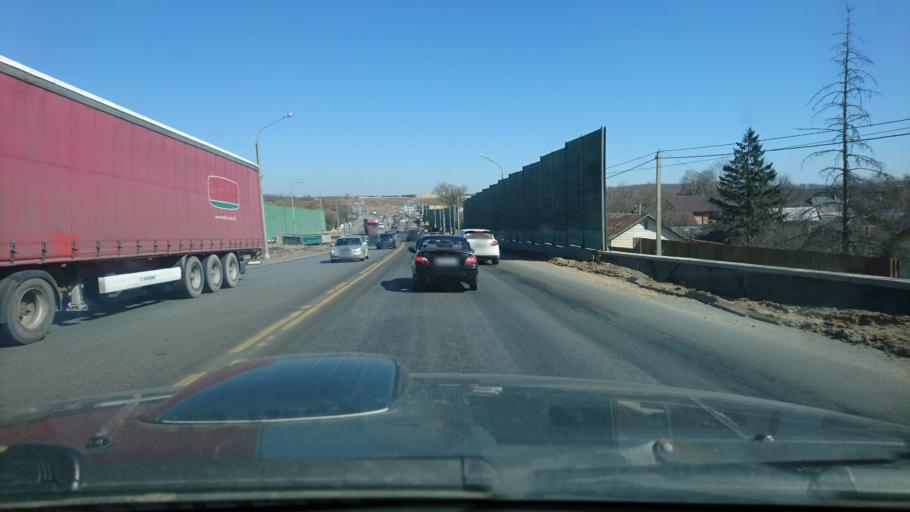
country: RU
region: Moskovskaya
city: Troitsk
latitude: 55.4355
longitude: 37.2834
